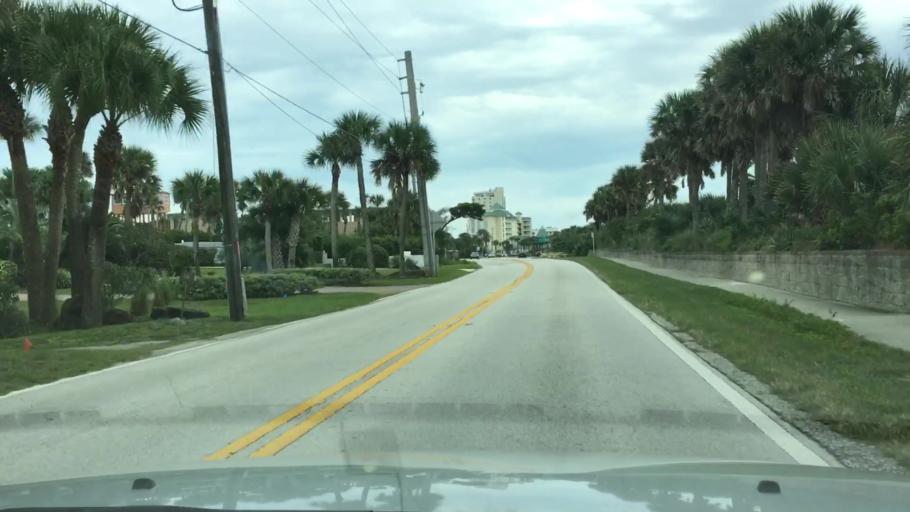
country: US
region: Florida
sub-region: Volusia County
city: Ormond Beach
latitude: 29.2952
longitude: -81.0415
